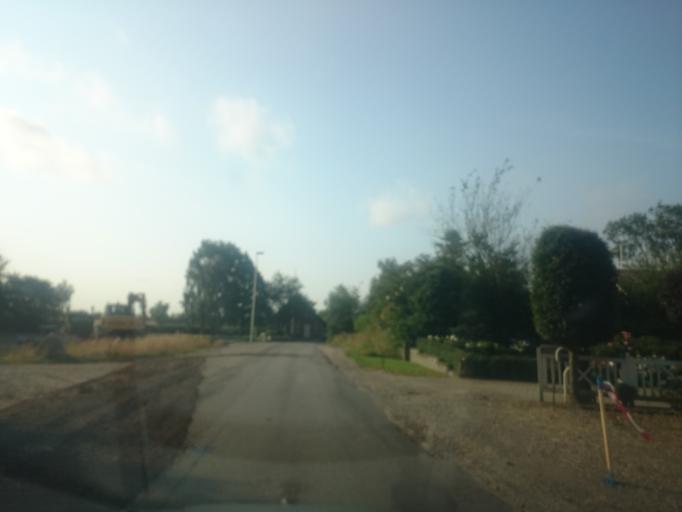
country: DK
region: South Denmark
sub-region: Vejle Kommune
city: Egtved
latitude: 55.6954
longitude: 9.3087
